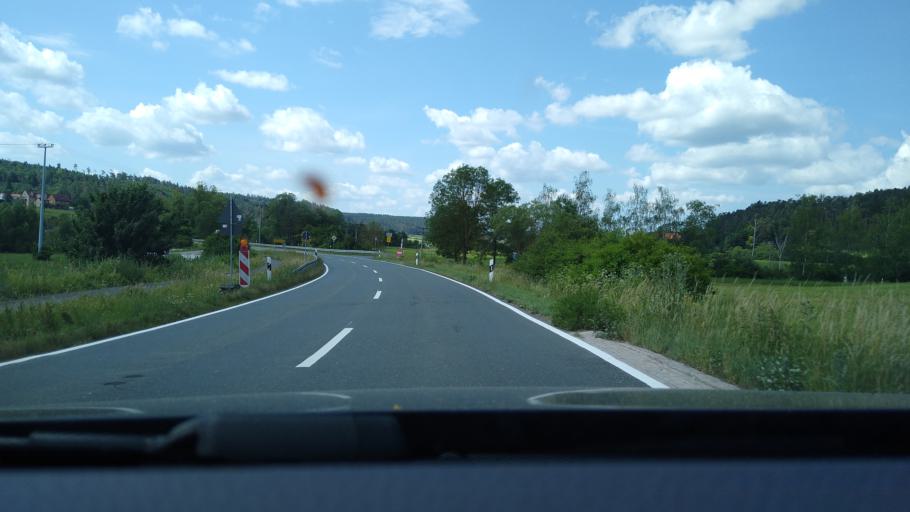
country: DE
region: Bavaria
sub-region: Regierungsbezirk Mittelfranken
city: Adelsdorf
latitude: 49.4739
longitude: 10.6850
